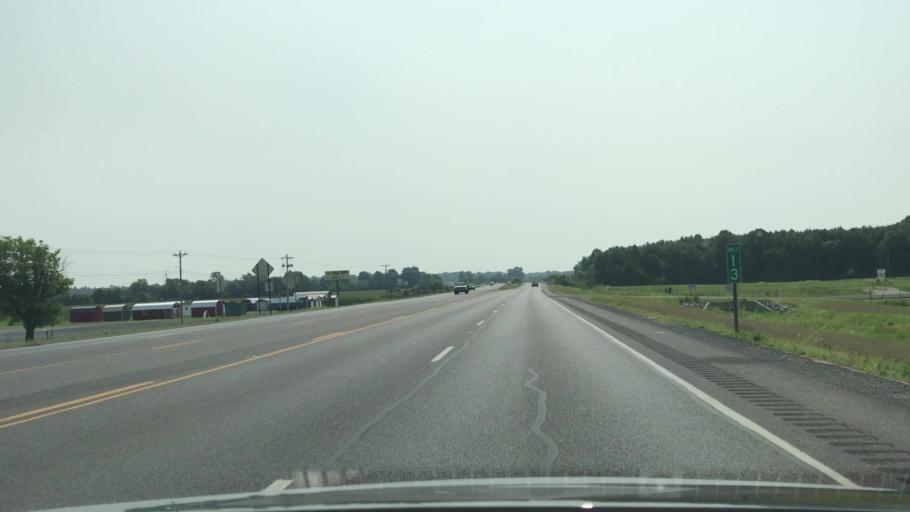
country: US
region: Kentucky
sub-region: Graves County
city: Mayfield
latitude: 36.7152
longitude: -88.6210
